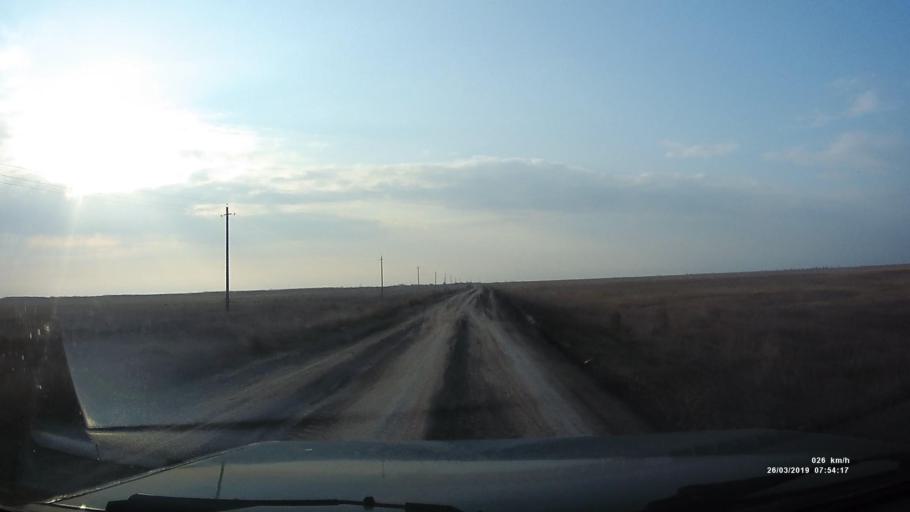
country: RU
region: Krasnodarskiy
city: Shabel'skoye
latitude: 47.1330
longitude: 38.5511
